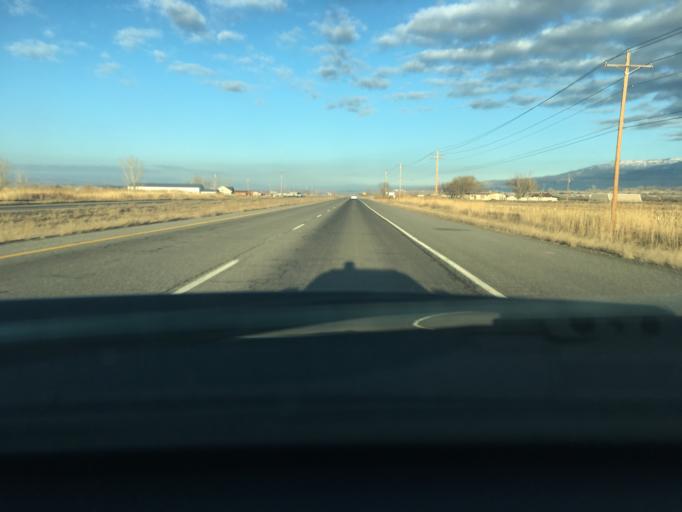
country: US
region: Colorado
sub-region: Delta County
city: Delta
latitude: 38.6944
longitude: -108.0201
